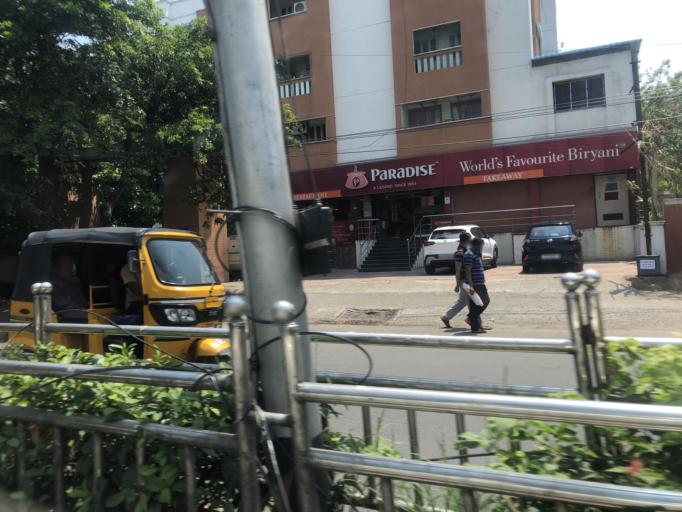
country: IN
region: Tamil Nadu
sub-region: Chennai
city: Gandhi Nagar
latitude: 12.9903
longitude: 80.2560
